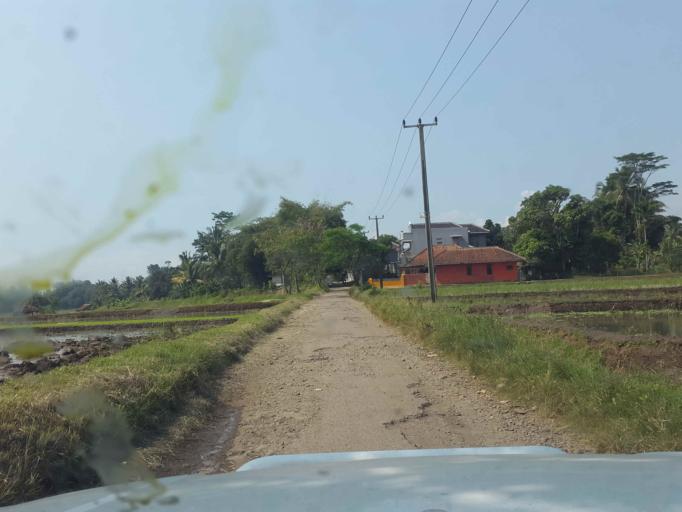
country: ID
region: West Java
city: Ciranjang-hilir
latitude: -6.8654
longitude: 107.2333
